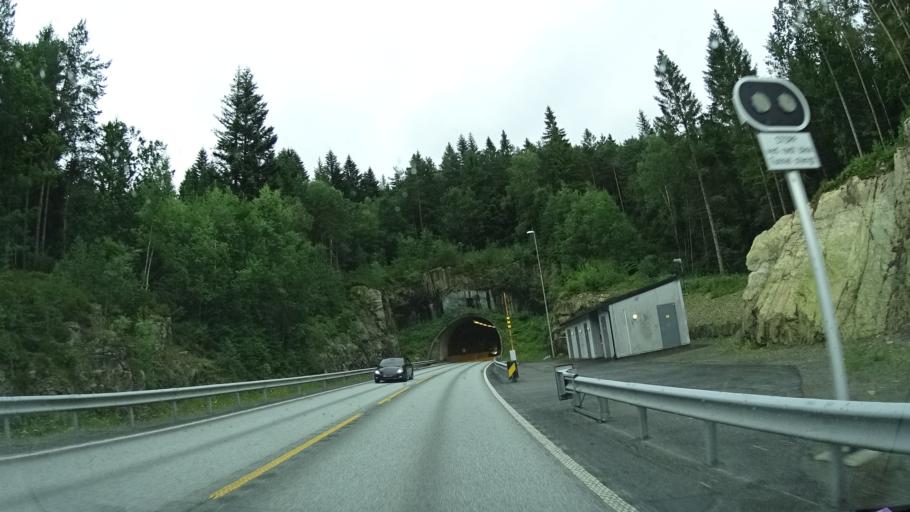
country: NO
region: Vest-Agder
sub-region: Flekkefjord
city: Flekkefjord
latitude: 58.3099
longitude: 6.6830
